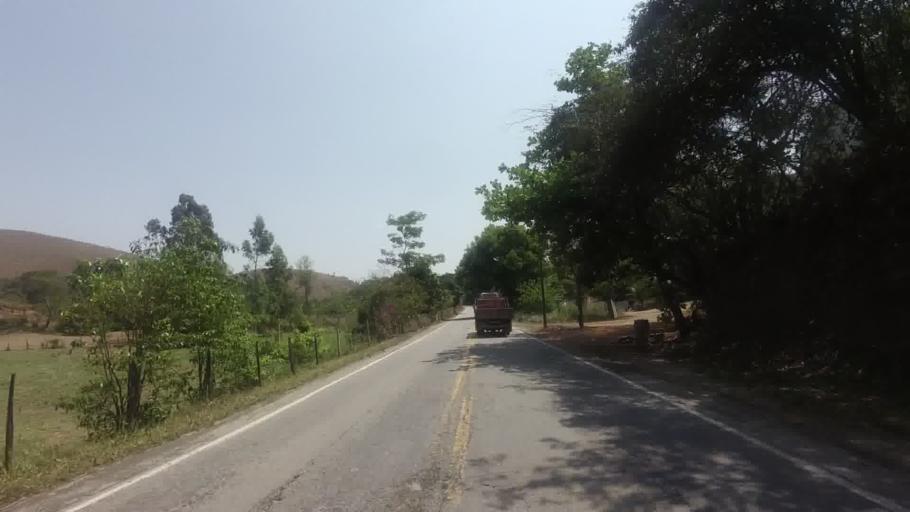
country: BR
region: Espirito Santo
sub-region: Rio Novo Do Sul
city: Rio Novo do Sul
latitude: -20.8816
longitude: -41.0092
